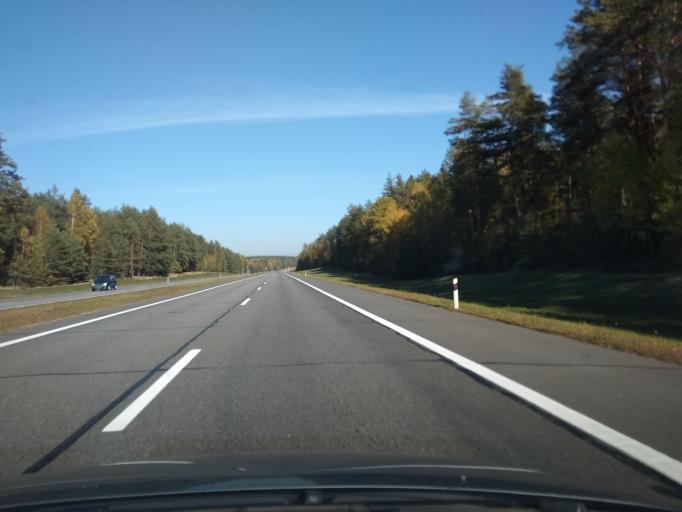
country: BY
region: Brest
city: Baranovichi
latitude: 53.0147
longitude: 25.7814
